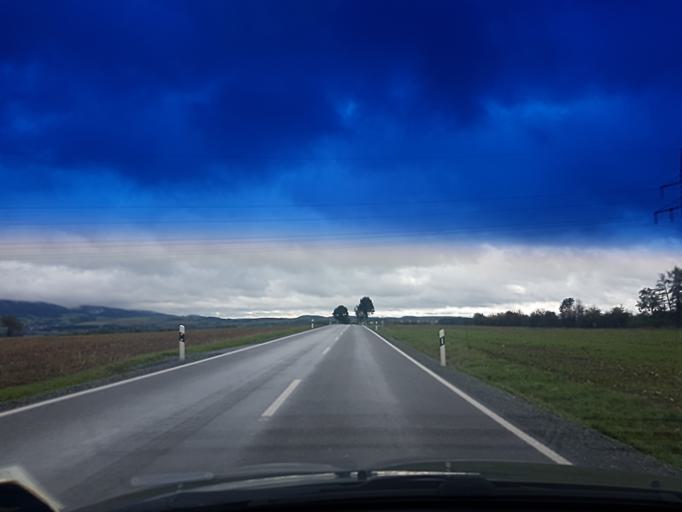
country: DE
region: Bavaria
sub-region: Upper Franconia
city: Bindlach
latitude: 50.0131
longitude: 11.6118
